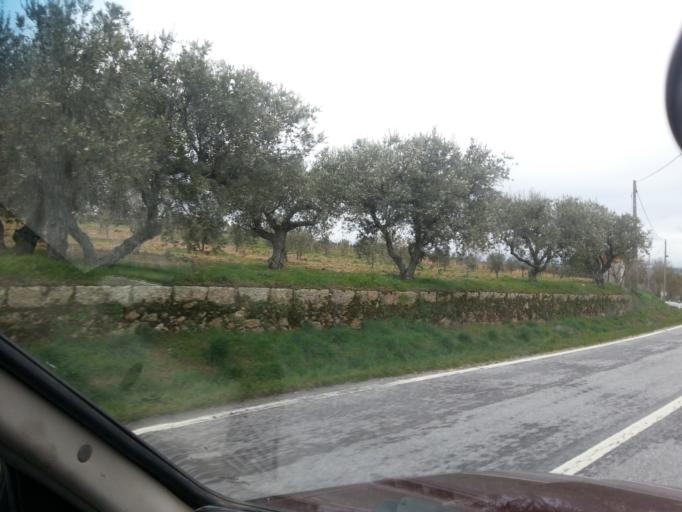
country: PT
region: Guarda
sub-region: Fornos de Algodres
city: Fornos de Algodres
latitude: 40.5636
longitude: -7.4744
